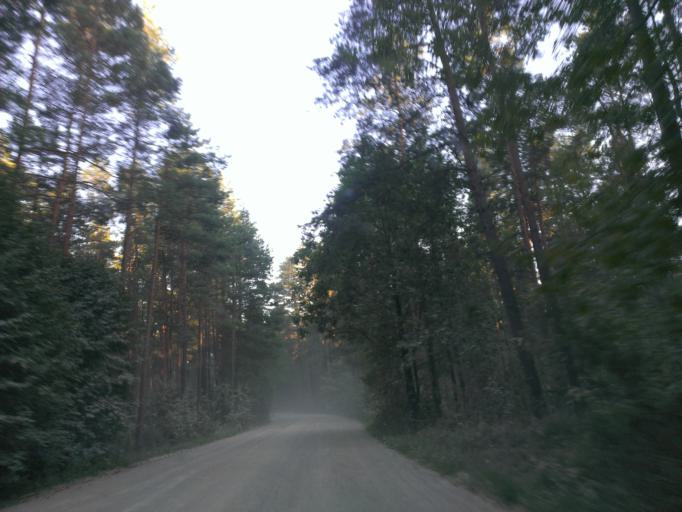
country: LV
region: Garkalne
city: Garkalne
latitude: 57.0625
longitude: 24.4112
